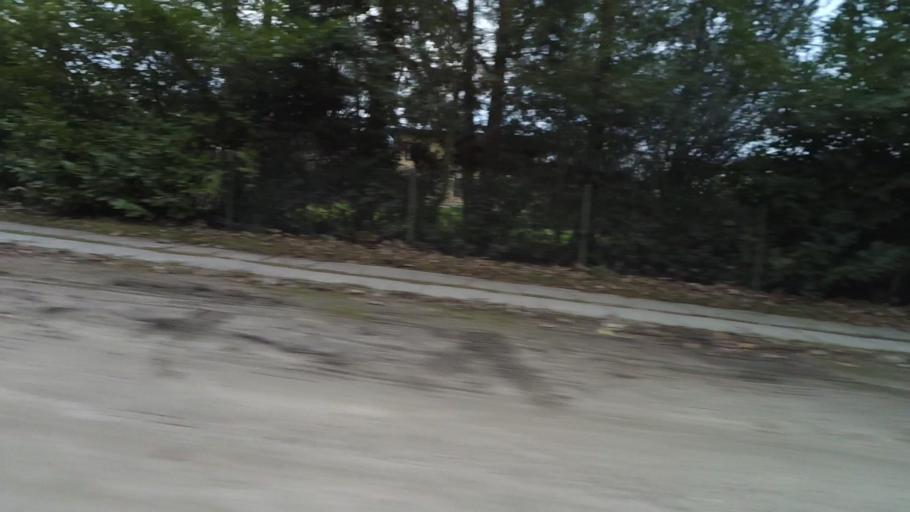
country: DK
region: Central Jutland
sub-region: Arhus Kommune
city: Stavtrup
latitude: 56.1565
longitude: 10.1187
